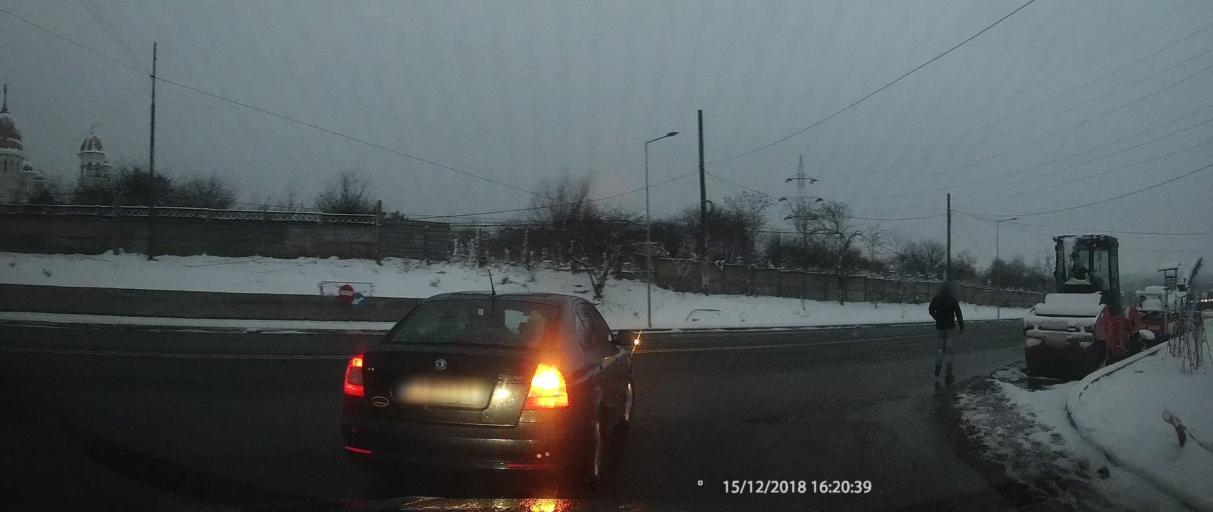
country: RO
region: Galati
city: Galati
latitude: 45.4136
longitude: 28.0050
